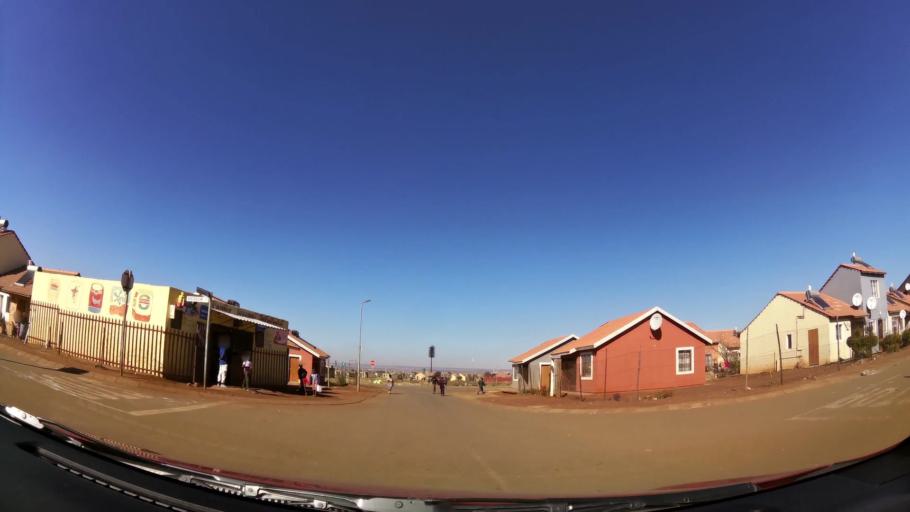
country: ZA
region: Gauteng
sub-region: City of Johannesburg Metropolitan Municipality
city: Soweto
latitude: -26.2361
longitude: 27.8003
